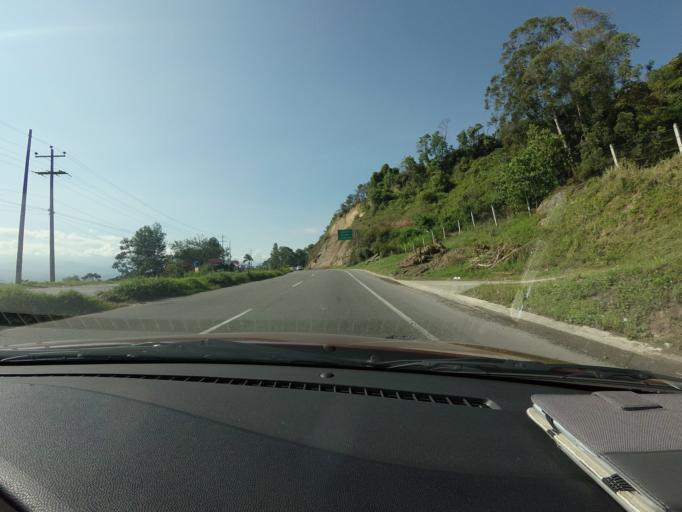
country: CO
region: Cundinamarca
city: Silvania
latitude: 4.4230
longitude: -74.3882
